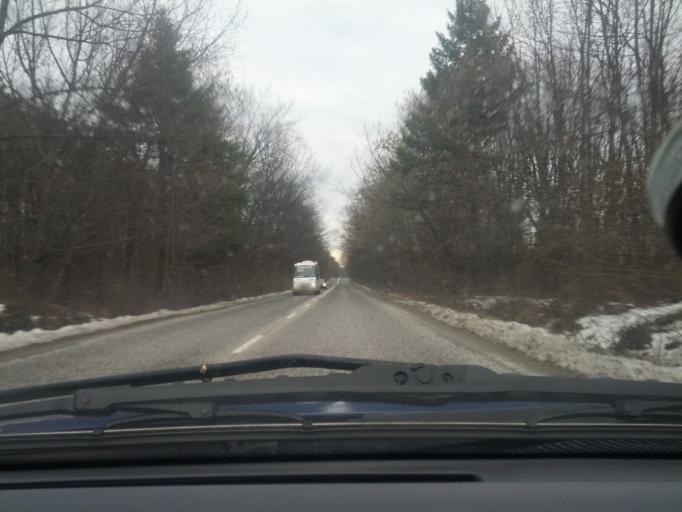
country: BG
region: Vratsa
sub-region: Obshtina Vratsa
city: Vratsa
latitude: 43.2807
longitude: 23.6281
